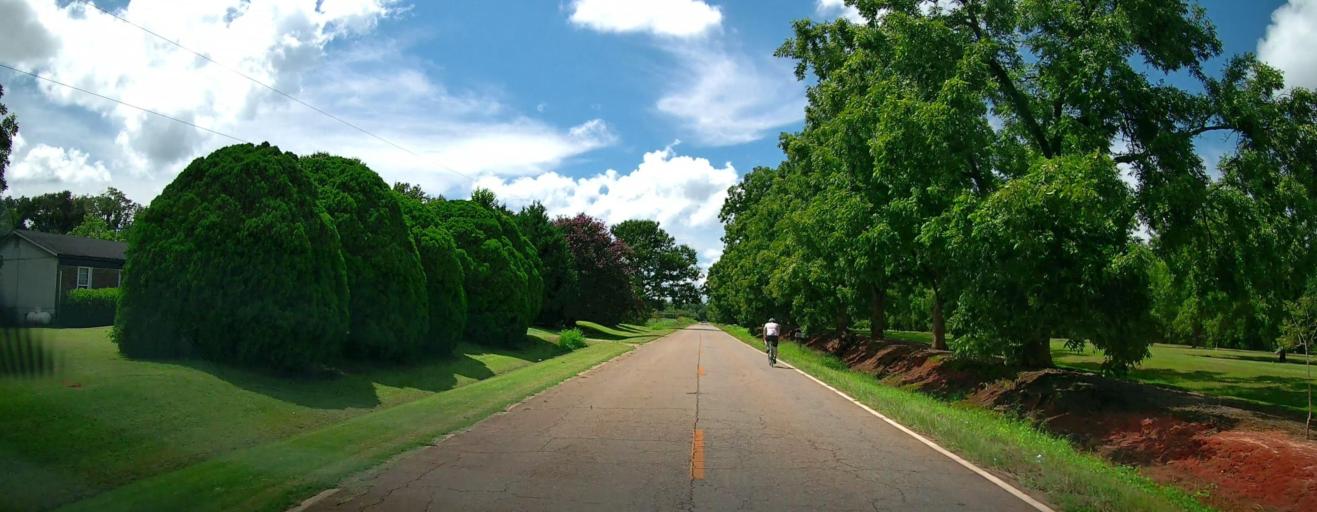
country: US
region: Georgia
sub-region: Houston County
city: Perry
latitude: 32.5211
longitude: -83.7795
